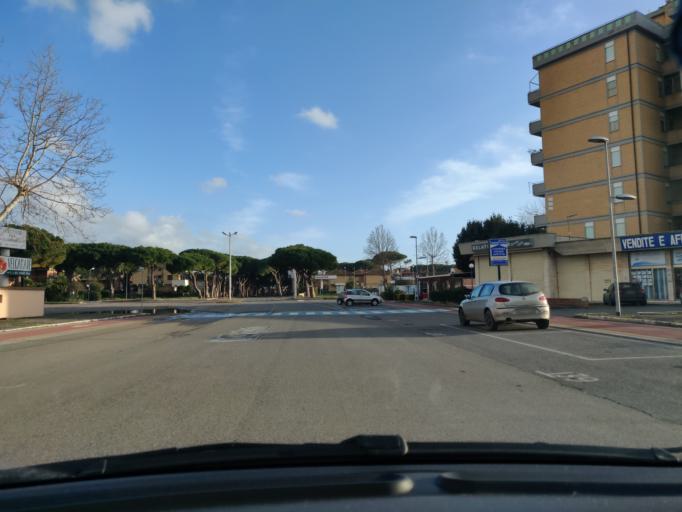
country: IT
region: Latium
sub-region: Provincia di Viterbo
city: Tarquinia
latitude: 42.2216
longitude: 11.7091
